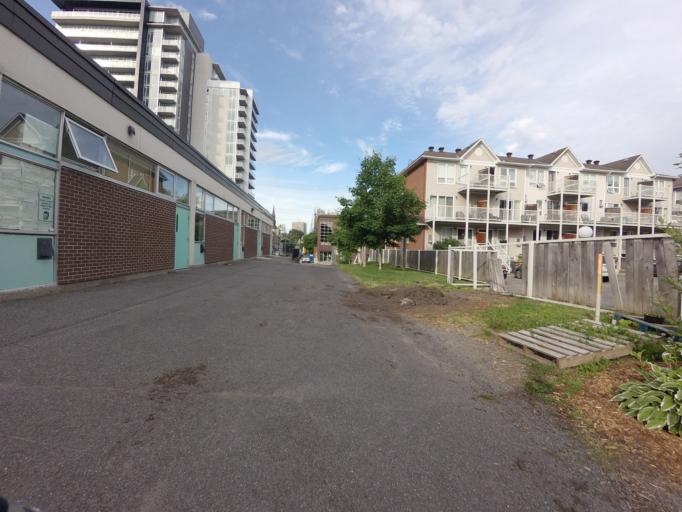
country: CA
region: Ontario
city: Ottawa
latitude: 45.4146
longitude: -75.7043
